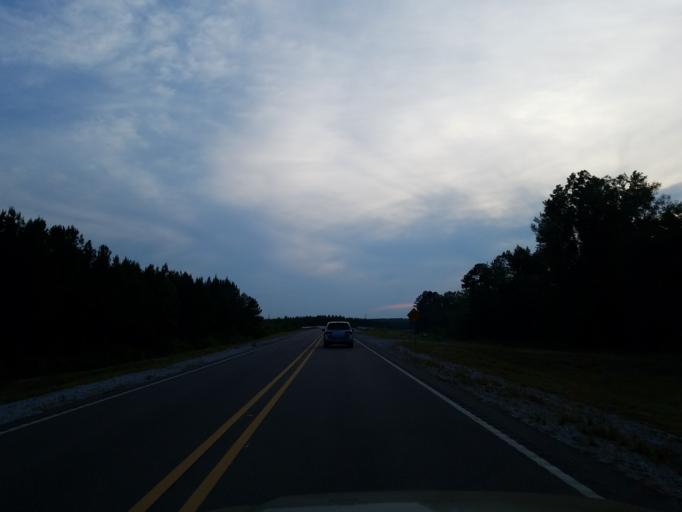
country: US
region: Mississippi
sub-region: Clarke County
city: Stonewall
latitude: 32.1965
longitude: -88.8083
